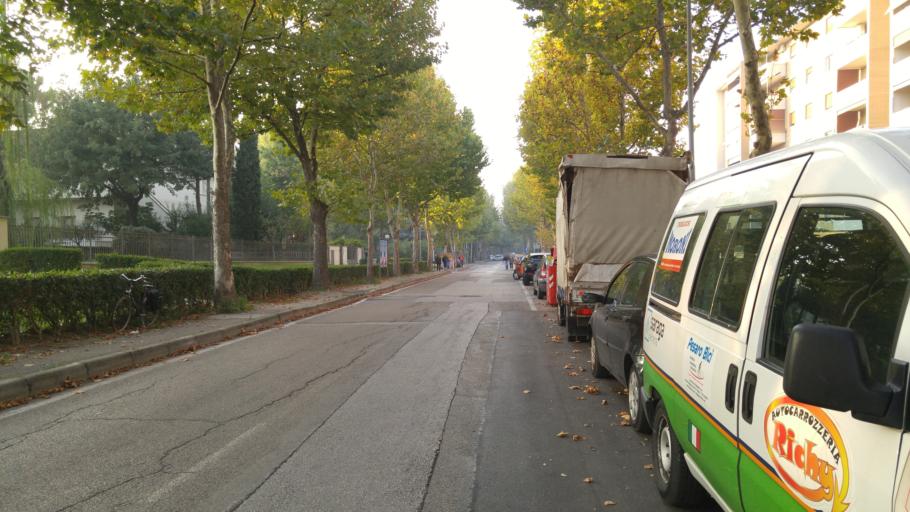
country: IT
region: The Marches
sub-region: Provincia di Pesaro e Urbino
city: Pesaro
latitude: 43.8975
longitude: 12.8881
